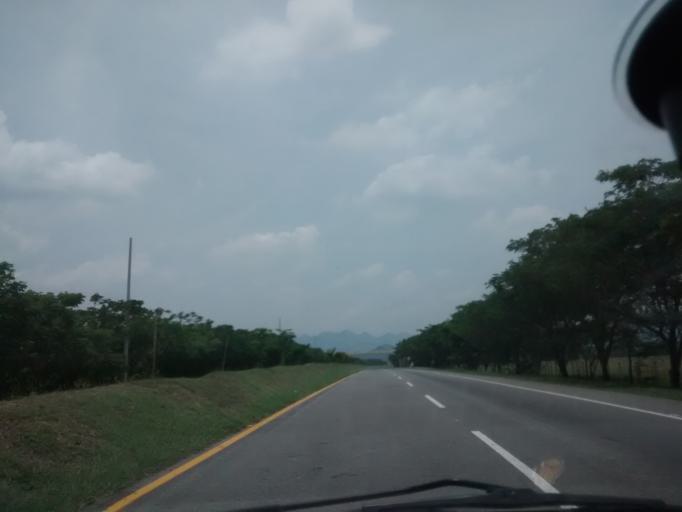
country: CO
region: Tolima
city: Espinal
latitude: 4.2315
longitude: -74.9774
